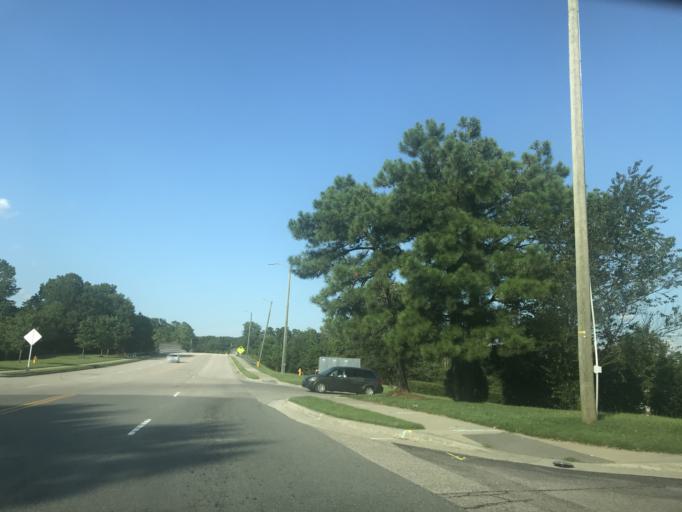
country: US
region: North Carolina
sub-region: Wake County
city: Knightdale
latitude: 35.7728
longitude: -78.5505
